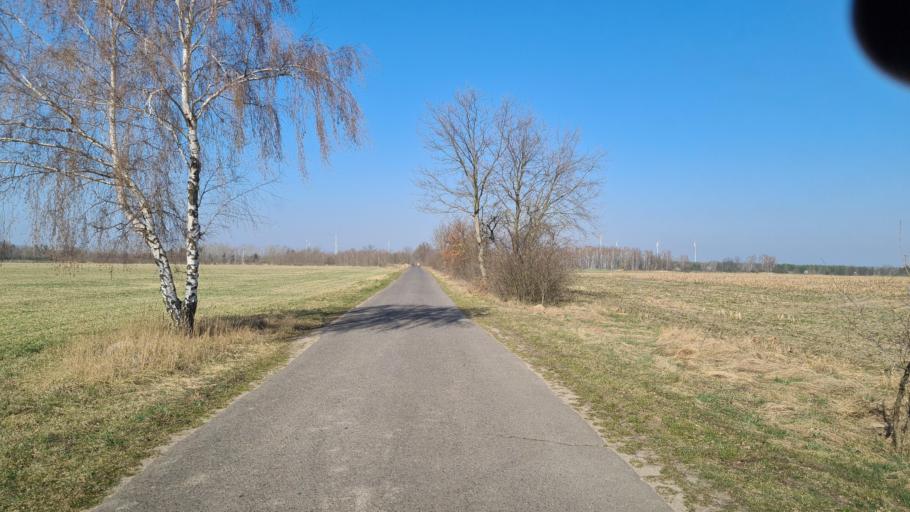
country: DE
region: Brandenburg
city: Calau
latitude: 51.7947
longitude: 13.9864
